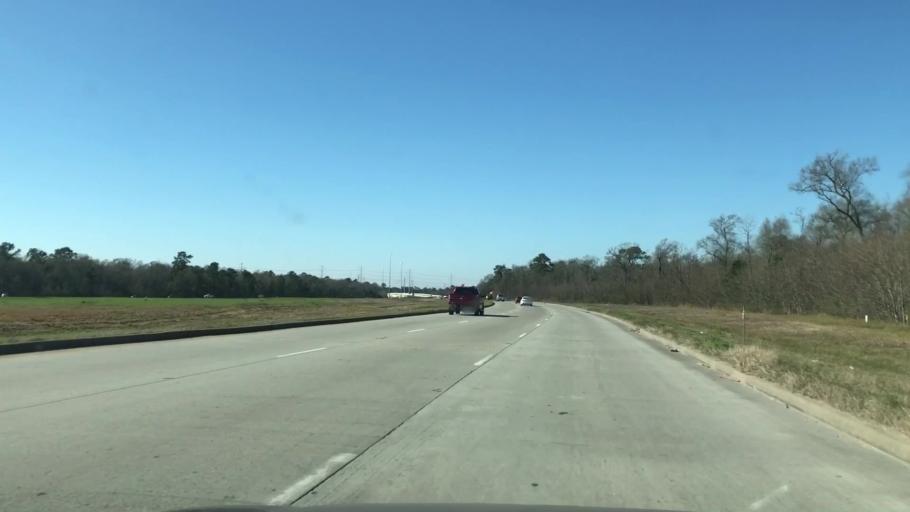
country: US
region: Texas
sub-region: Harris County
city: Cloverleaf
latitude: 29.8257
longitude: -95.1930
